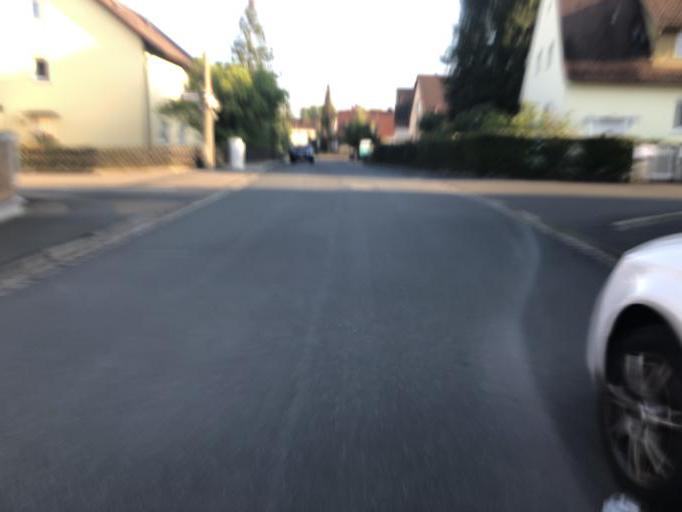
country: DE
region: Bavaria
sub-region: Regierungsbezirk Mittelfranken
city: Erlangen
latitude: 49.5990
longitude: 10.9836
